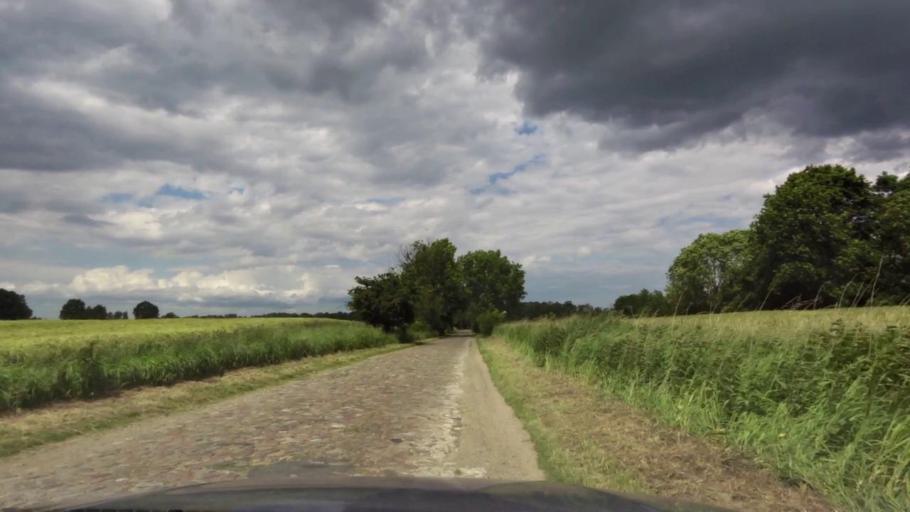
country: PL
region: West Pomeranian Voivodeship
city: Trzcinsko Zdroj
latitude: 52.9561
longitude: 14.7135
